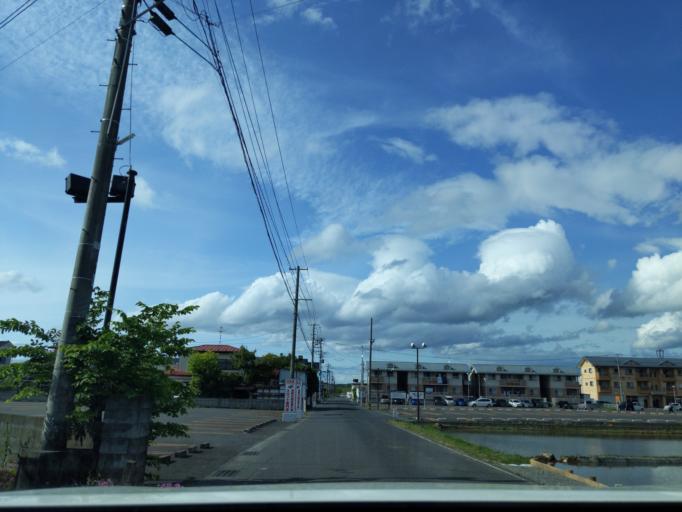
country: JP
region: Fukushima
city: Sukagawa
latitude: 37.2955
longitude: 140.3808
